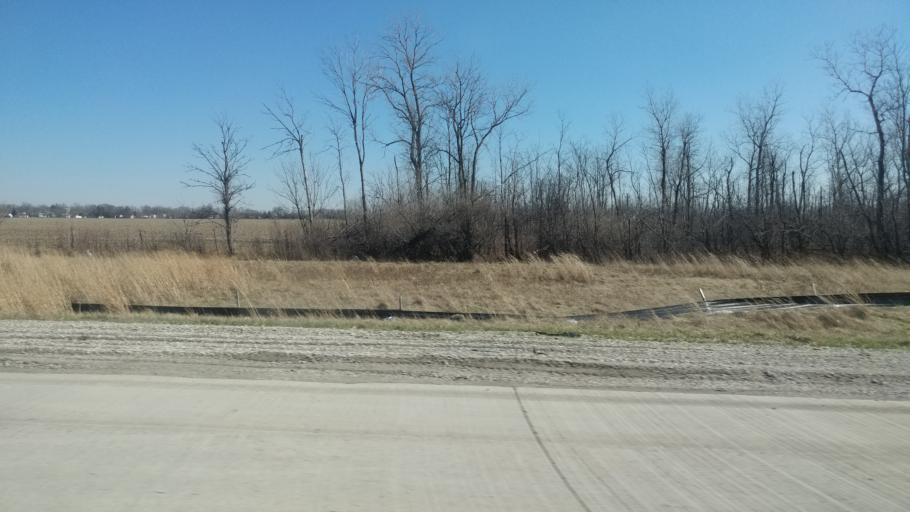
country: US
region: Ohio
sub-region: Wood County
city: Bowling Green
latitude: 41.4515
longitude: -83.6222
